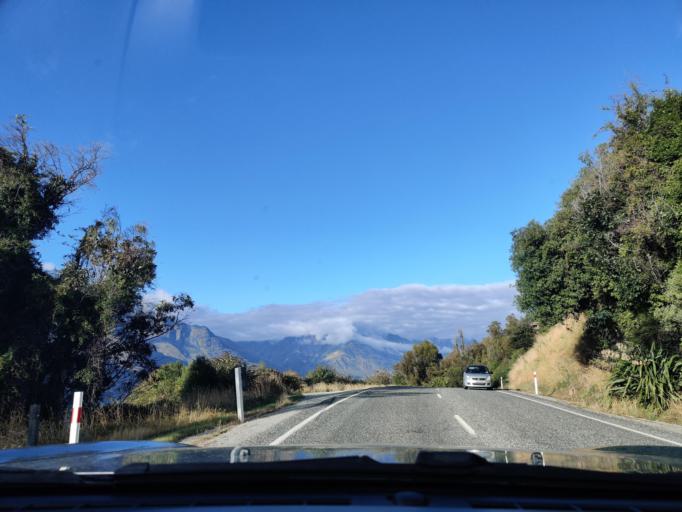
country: NZ
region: Otago
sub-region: Queenstown-Lakes District
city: Queenstown
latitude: -45.0419
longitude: 168.6360
